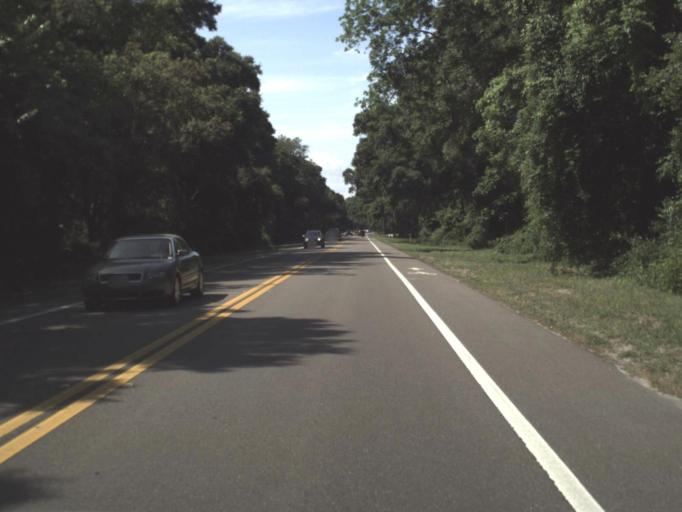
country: US
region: Florida
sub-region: Nassau County
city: Fernandina Beach
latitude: 30.5602
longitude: -81.4513
